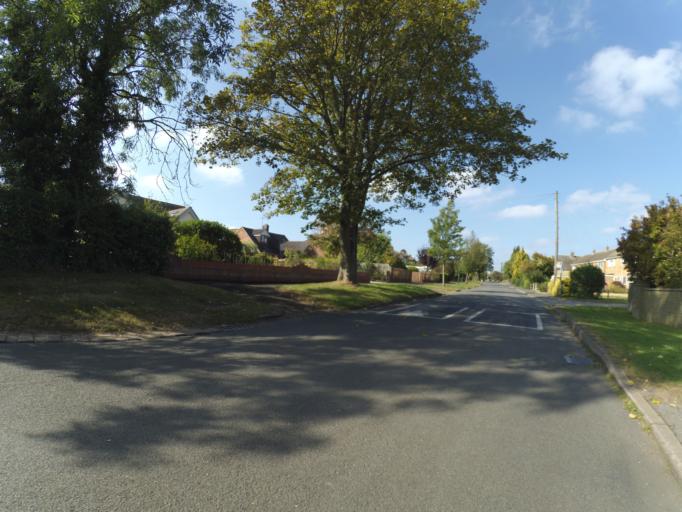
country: GB
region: England
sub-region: Warwickshire
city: Rugby
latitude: 52.3813
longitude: -1.2188
